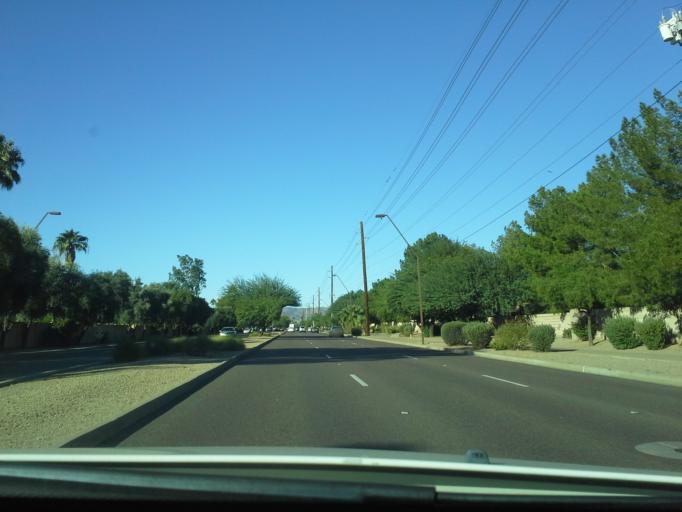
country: US
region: Arizona
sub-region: Maricopa County
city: San Carlos
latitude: 33.3493
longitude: -111.9034
